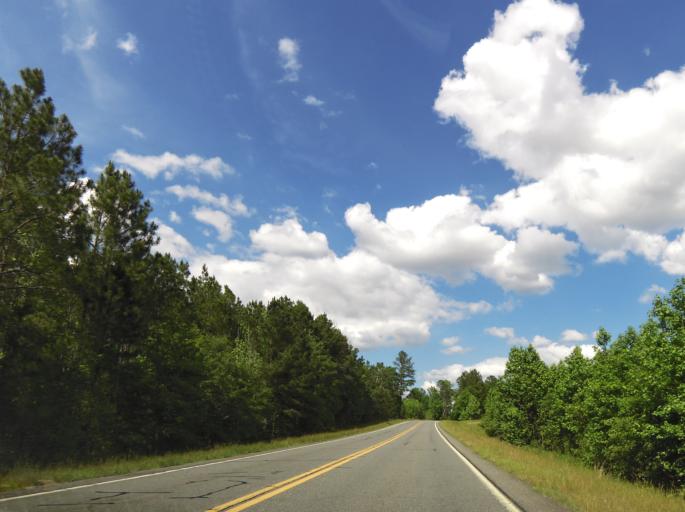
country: US
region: Georgia
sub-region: Treutlen County
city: Soperton
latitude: 32.3456
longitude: -82.6467
